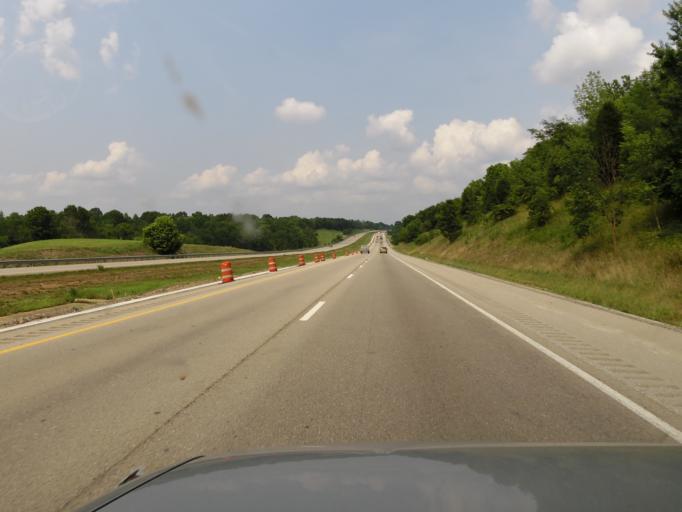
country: US
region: Kentucky
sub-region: Boone County
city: Verona
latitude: 38.8194
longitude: -84.7015
